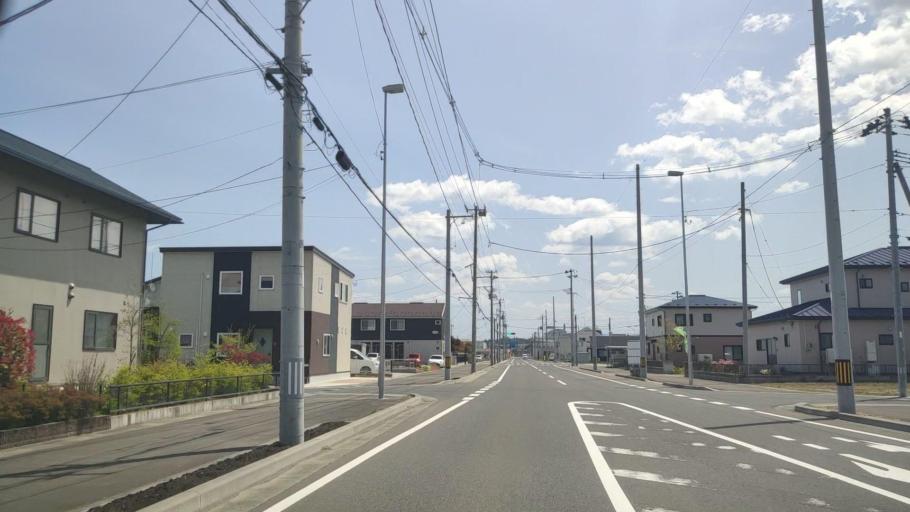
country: JP
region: Aomori
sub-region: Hachinohe Shi
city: Uchimaru
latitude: 40.5153
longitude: 141.4303
